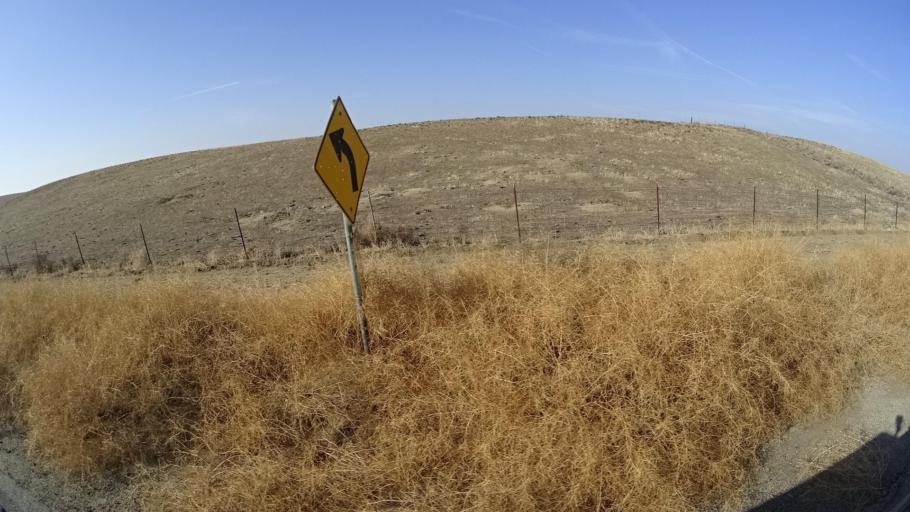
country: US
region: California
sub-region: Tulare County
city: Richgrove
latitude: 35.6244
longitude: -119.0302
